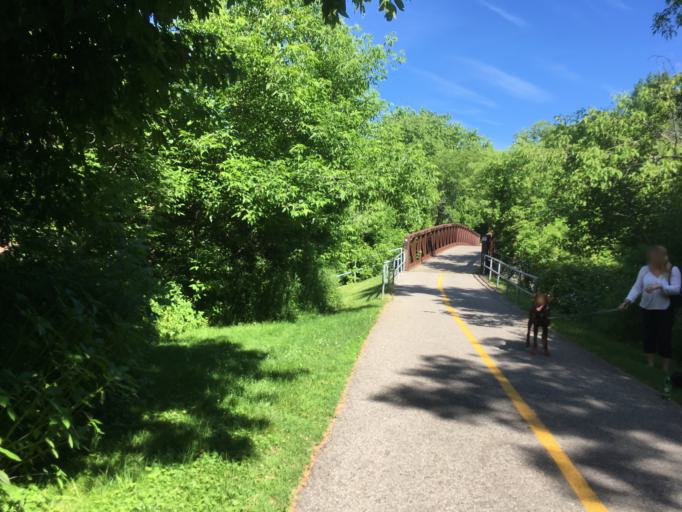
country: CA
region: Ontario
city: Oshawa
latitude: 43.8768
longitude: -78.8553
